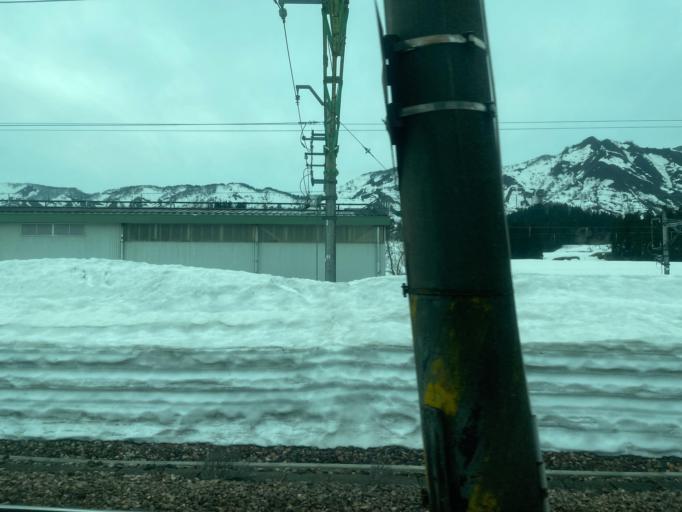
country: JP
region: Niigata
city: Shiozawa
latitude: 36.9910
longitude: 138.8041
